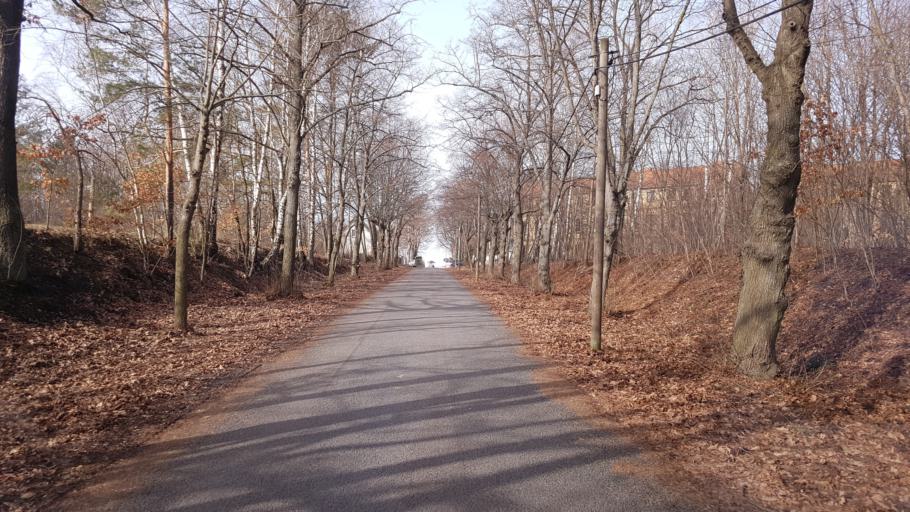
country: DE
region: Brandenburg
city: Schwarzheide
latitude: 51.5278
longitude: 13.8243
